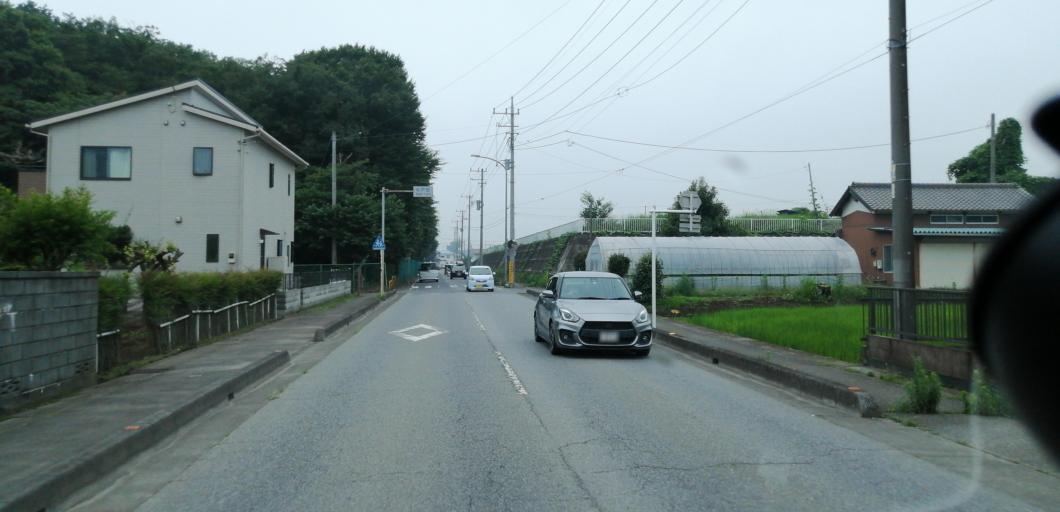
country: JP
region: Ibaraki
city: Sakai
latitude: 36.0402
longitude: 139.8058
